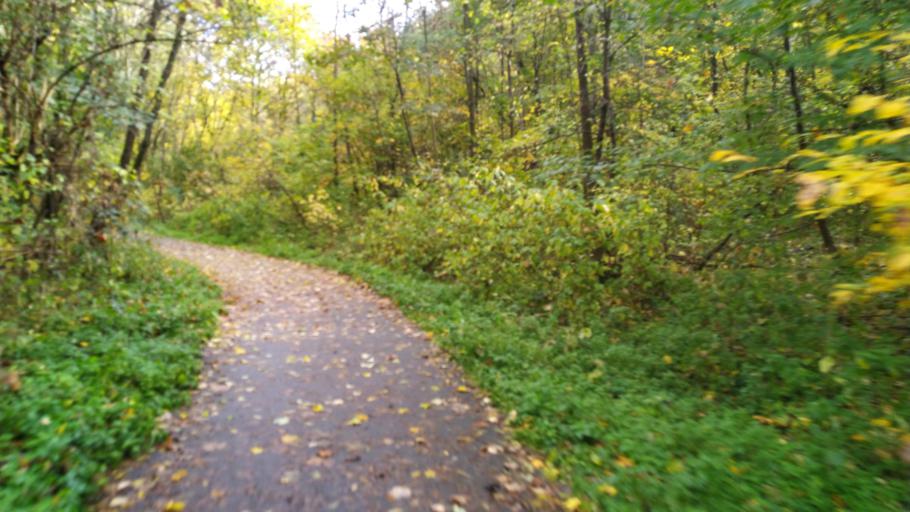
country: DE
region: Thuringia
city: Weimar
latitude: 50.9863
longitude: 11.3469
